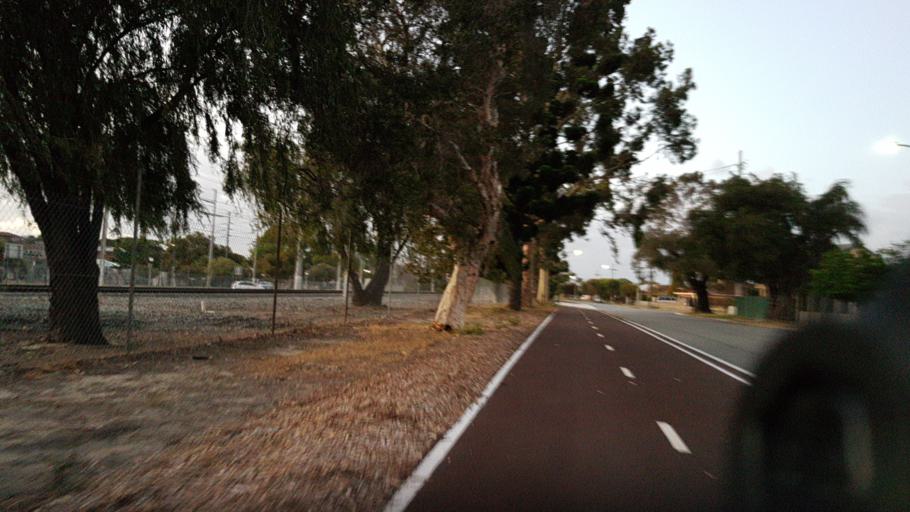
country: AU
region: Western Australia
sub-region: Victoria Park
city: East Victoria Park
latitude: -31.9862
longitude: 115.9157
